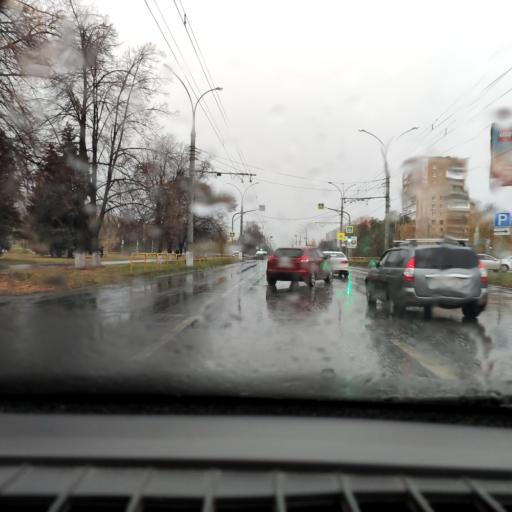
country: RU
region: Samara
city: Tol'yatti
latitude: 53.5306
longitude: 49.2766
